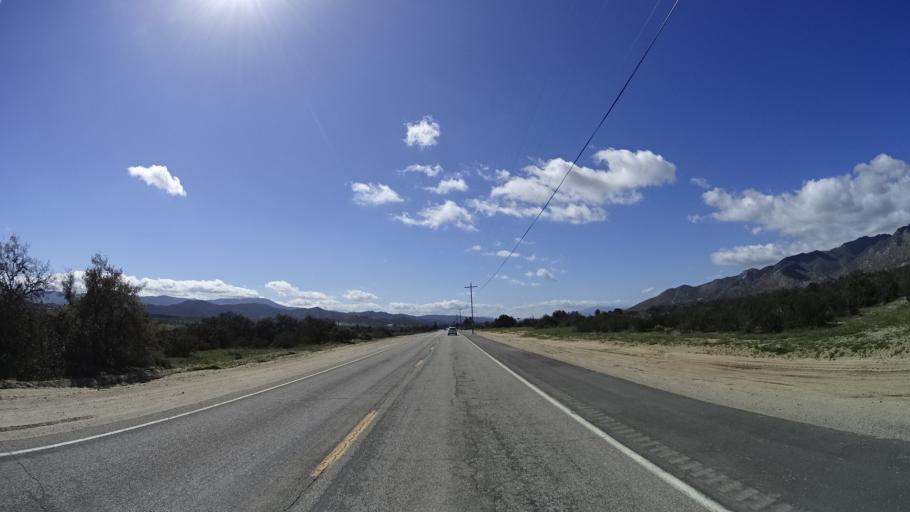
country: US
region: California
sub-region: San Diego County
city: Borrego Springs
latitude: 33.2104
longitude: -116.5114
